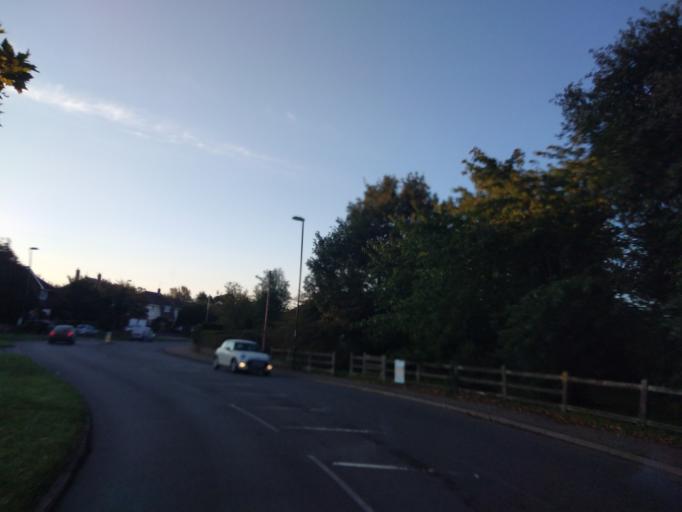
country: GB
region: England
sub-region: West Sussex
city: Littlehampton
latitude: 50.8171
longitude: -0.5291
